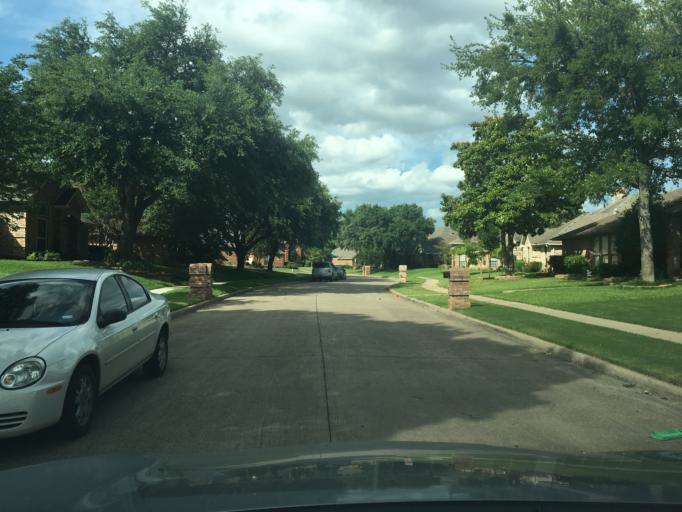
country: US
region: Texas
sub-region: Dallas County
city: Garland
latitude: 32.9329
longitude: -96.6723
